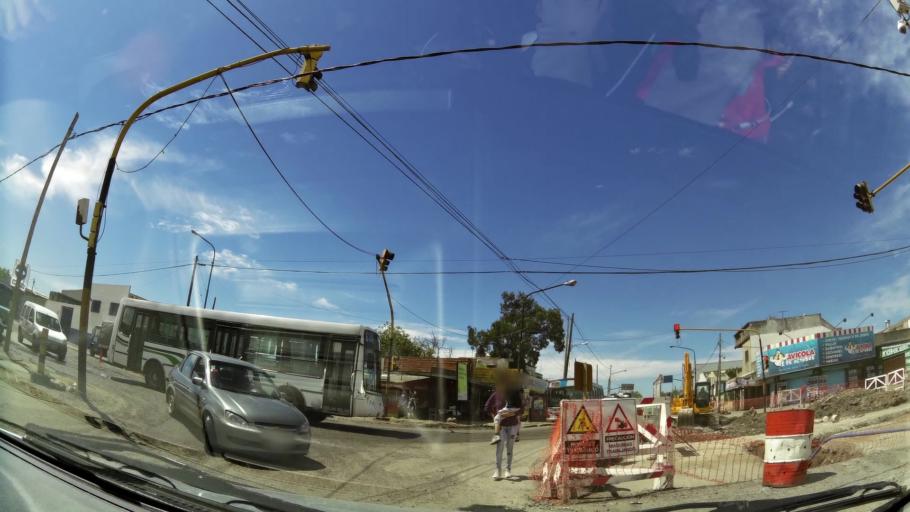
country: AR
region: Buenos Aires
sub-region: Partido de Quilmes
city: Quilmes
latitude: -34.7510
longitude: -58.3060
